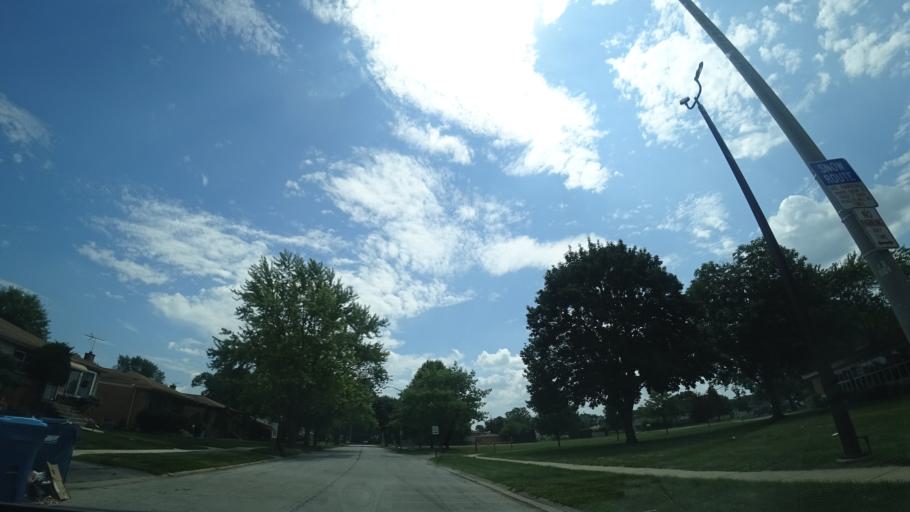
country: US
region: Illinois
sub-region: Cook County
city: Alsip
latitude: 41.6795
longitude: -87.7285
